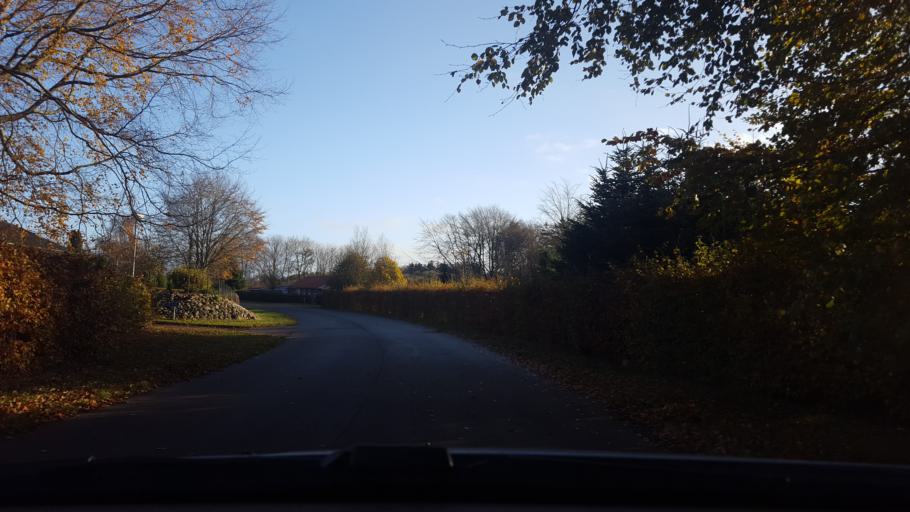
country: DK
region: North Denmark
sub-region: Morso Kommune
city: Nykobing Mors
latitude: 56.7536
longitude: 8.8781
